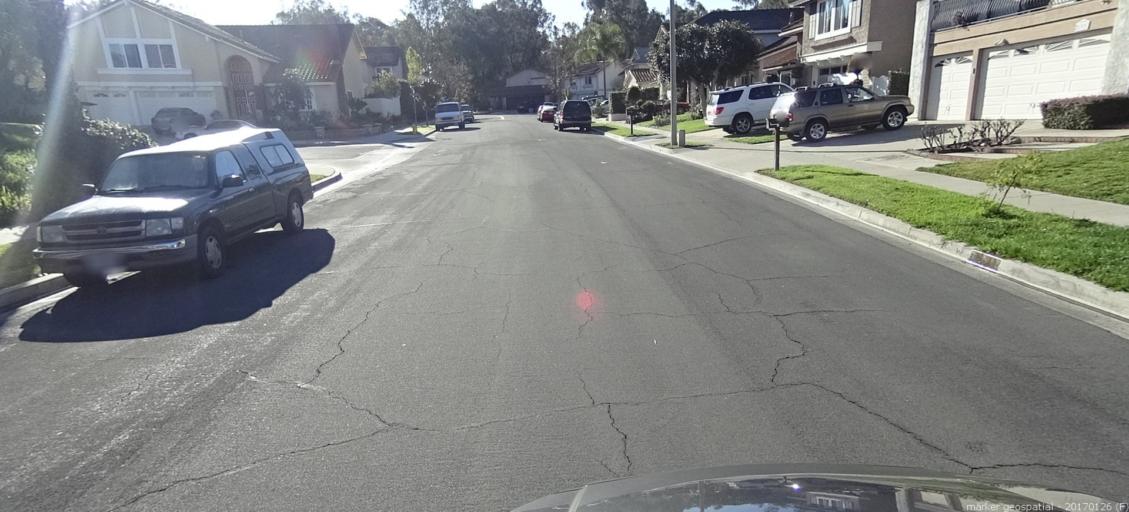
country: US
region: California
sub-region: Orange County
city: Lake Forest
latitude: 33.6444
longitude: -117.6954
